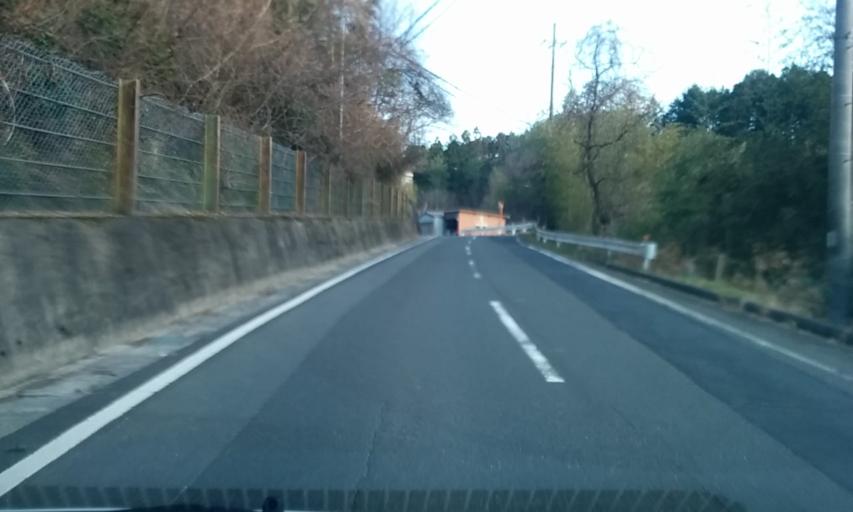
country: JP
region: Kyoto
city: Ayabe
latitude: 35.2884
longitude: 135.2433
